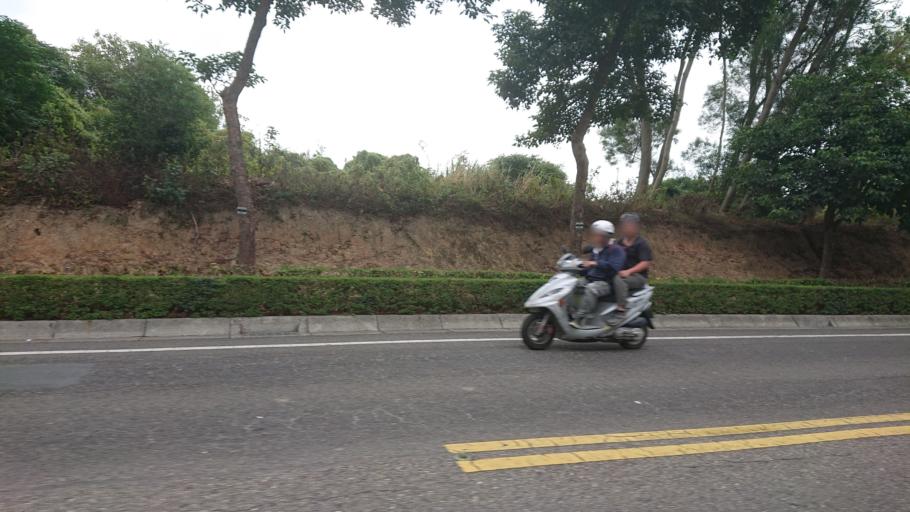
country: TW
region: Fukien
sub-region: Kinmen
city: Jincheng
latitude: 24.4151
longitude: 118.3053
